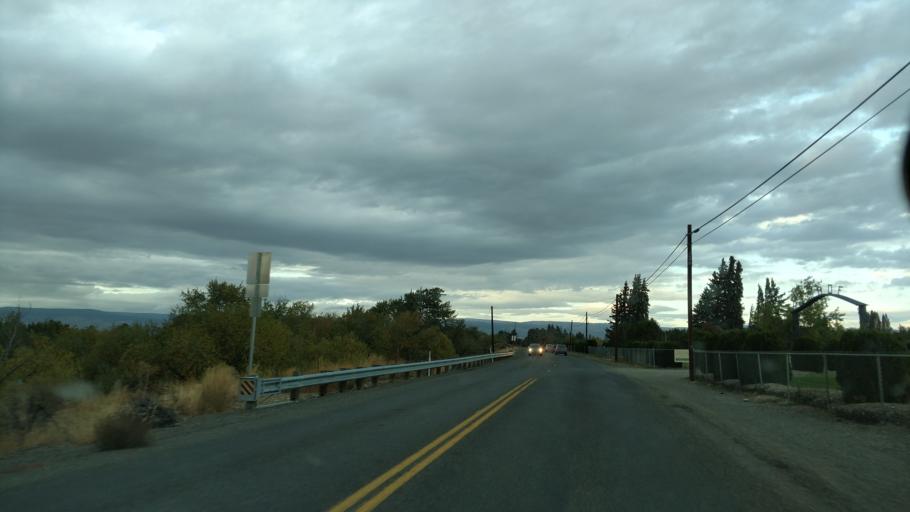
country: US
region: Washington
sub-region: Kittitas County
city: Ellensburg
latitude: 47.0095
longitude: -120.5231
